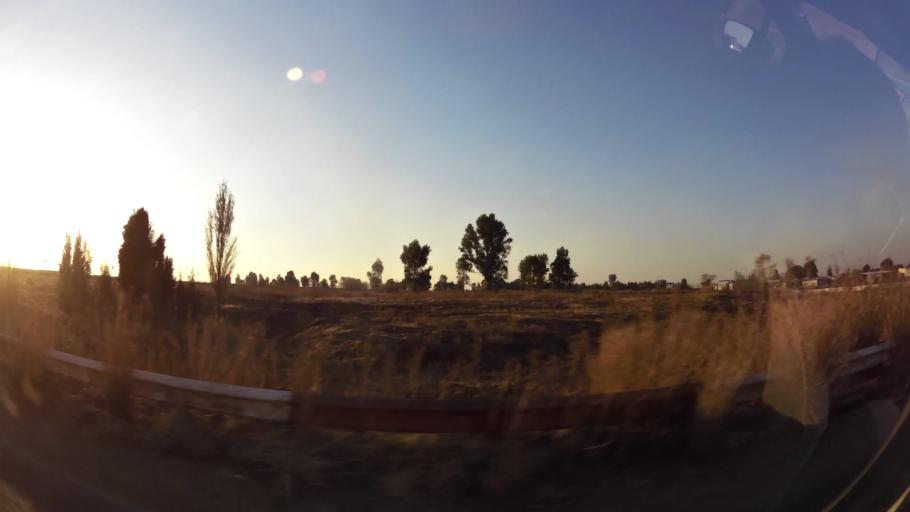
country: ZA
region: Gauteng
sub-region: West Rand District Municipality
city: Randfontein
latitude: -26.2021
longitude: 27.6768
